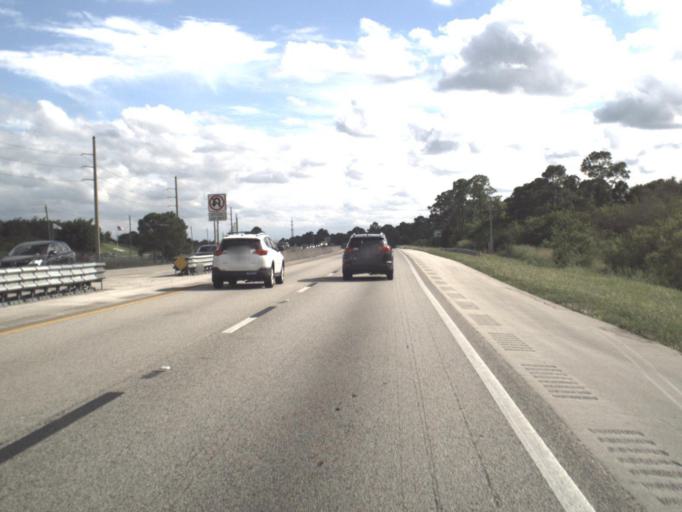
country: US
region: Florida
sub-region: Saint Lucie County
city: Port Saint Lucie
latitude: 27.2285
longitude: -80.3421
